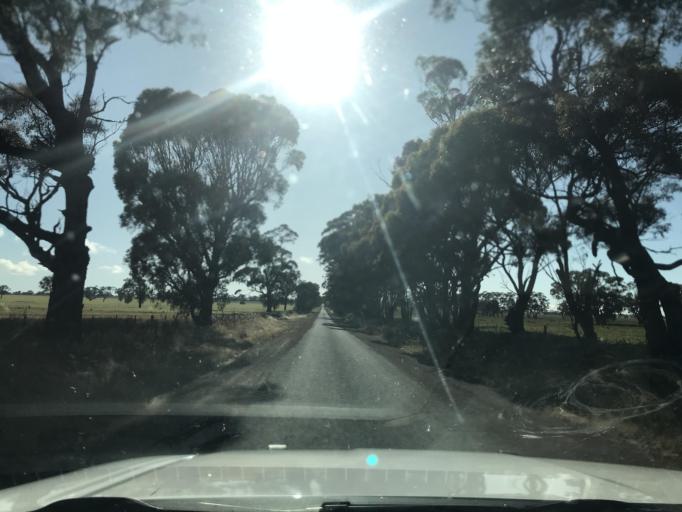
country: AU
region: Victoria
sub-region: Horsham
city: Horsham
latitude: -36.6932
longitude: 141.5560
